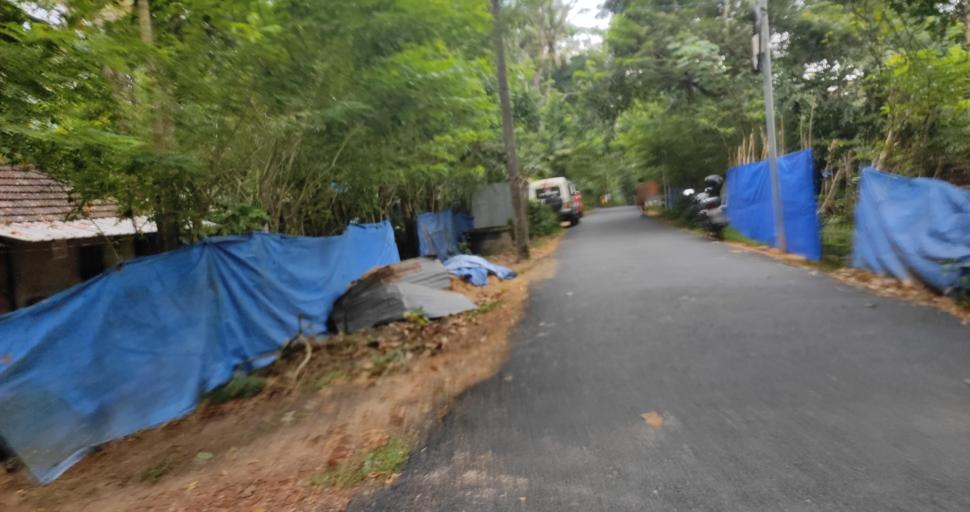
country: IN
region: Kerala
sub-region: Alappuzha
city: Shertallai
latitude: 9.6686
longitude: 76.3331
